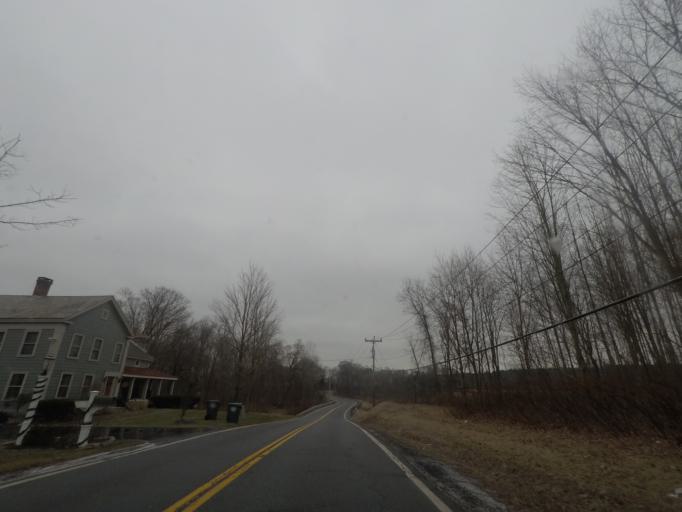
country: US
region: New York
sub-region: Saratoga County
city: Country Knolls
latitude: 42.9165
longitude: -73.7711
